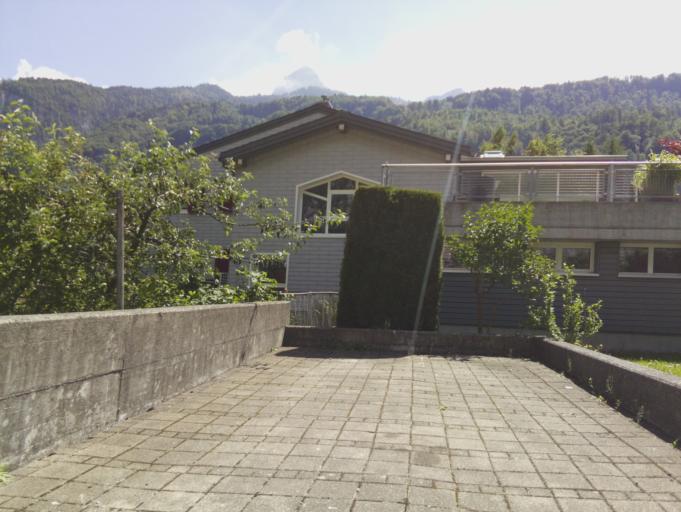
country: CH
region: Glarus
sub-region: Glarus
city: Netstal
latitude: 47.0667
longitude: 9.0560
